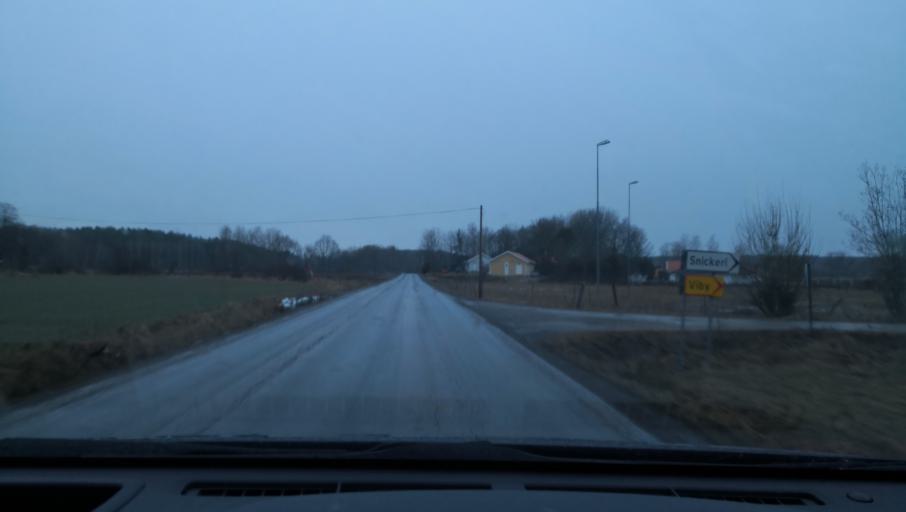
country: SE
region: Soedermanland
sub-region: Eskilstuna Kommun
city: Arla
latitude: 59.3905
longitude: 16.6533
